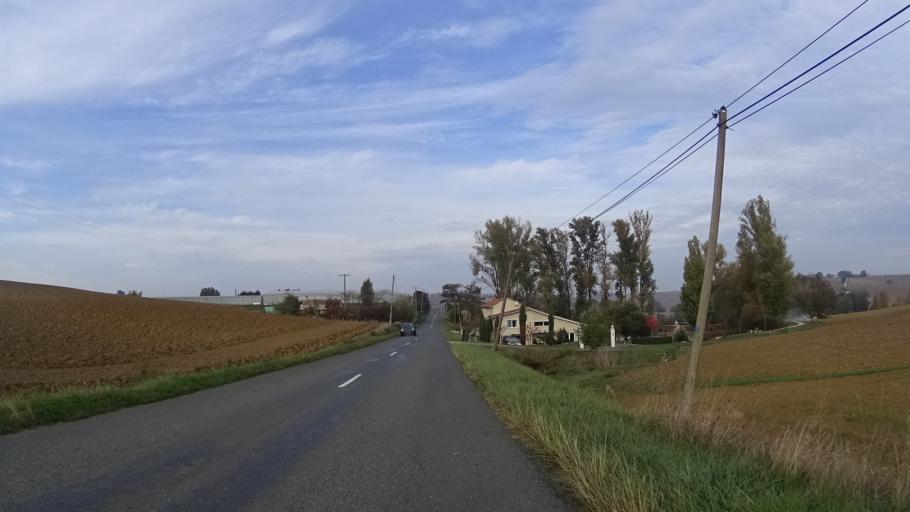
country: FR
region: Aquitaine
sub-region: Departement du Lot-et-Garonne
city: Laplume
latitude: 44.0996
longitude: 0.5595
